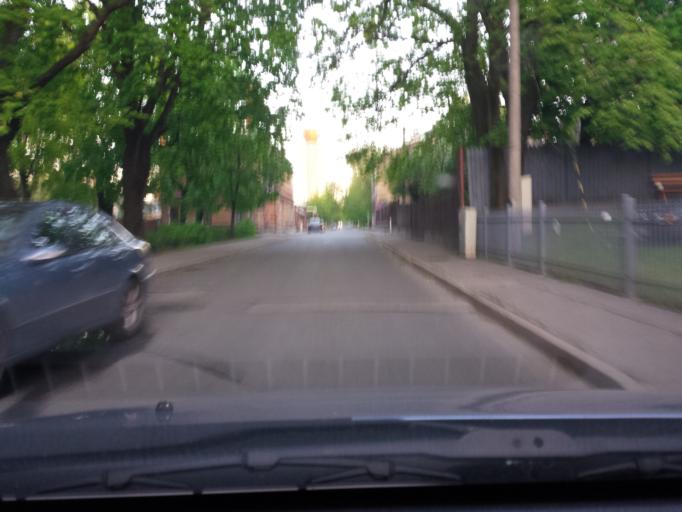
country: LV
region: Riga
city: Riga
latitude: 56.9939
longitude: 24.1282
